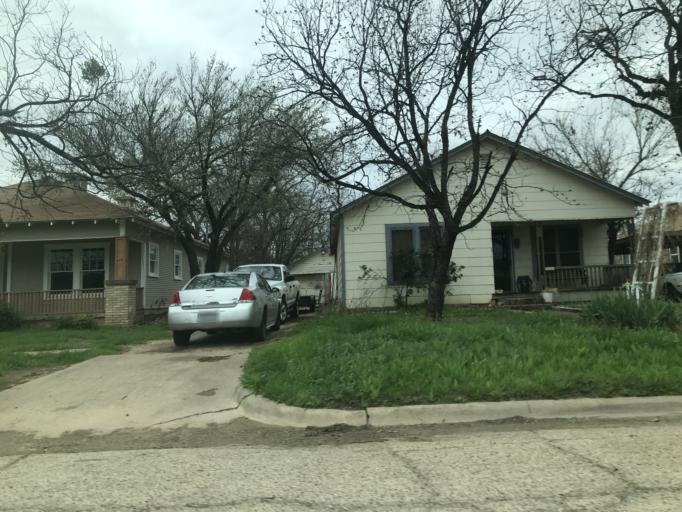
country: US
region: Texas
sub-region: Taylor County
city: Abilene
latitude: 32.4656
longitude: -99.7377
